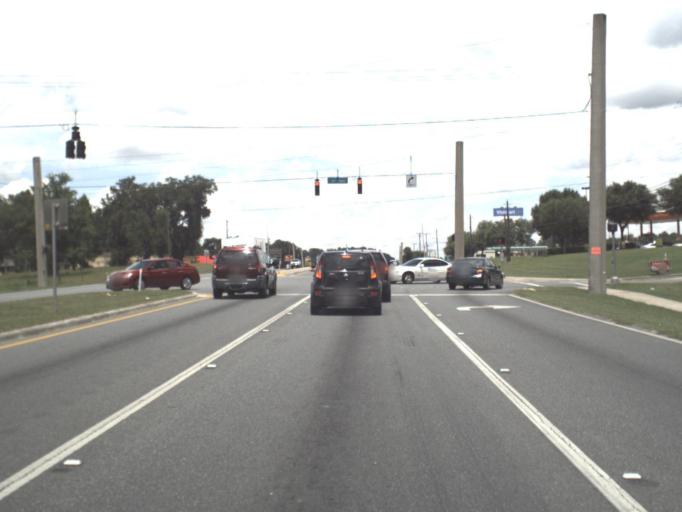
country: US
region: Florida
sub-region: Suwannee County
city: Live Oak
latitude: 30.3228
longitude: -82.9677
